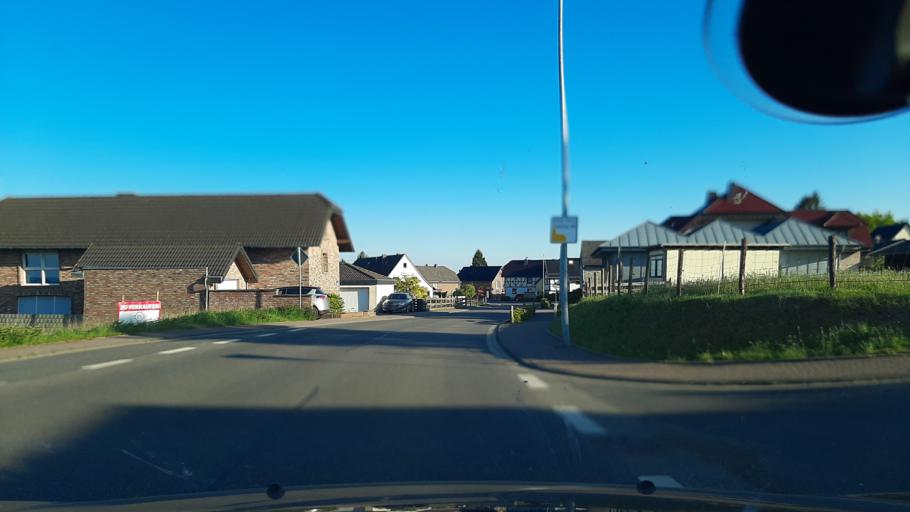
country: DE
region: Rheinland-Pfalz
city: Ohlenhard
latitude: 50.4758
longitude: 6.7133
